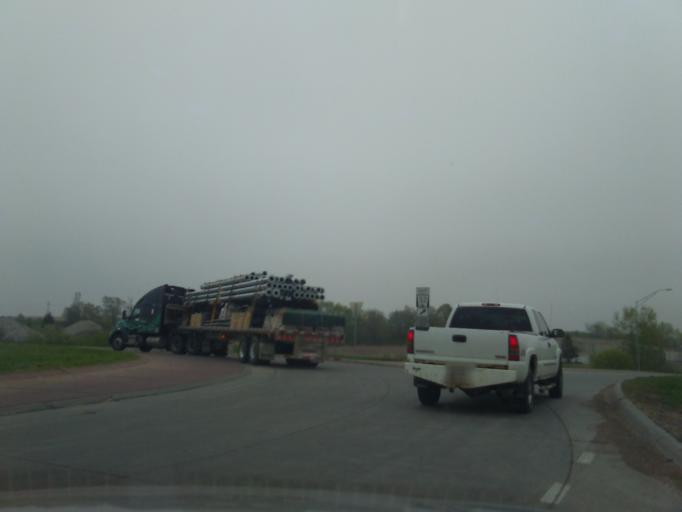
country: US
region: Nebraska
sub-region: Burt County
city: Oakland
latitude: 41.8241
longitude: -96.4662
